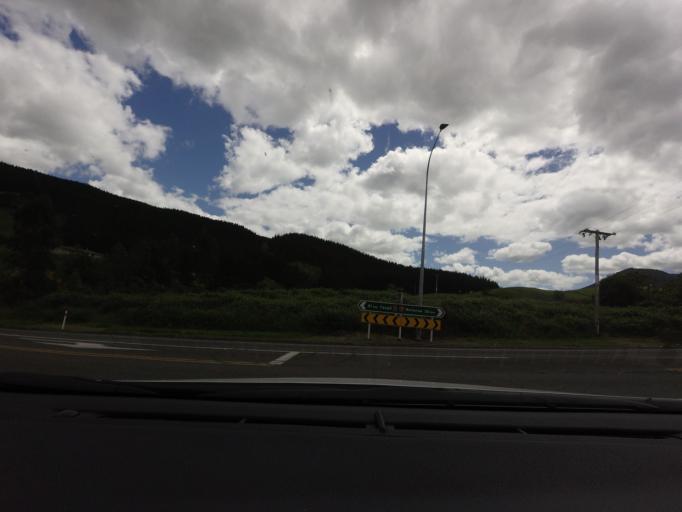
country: NZ
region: Bay of Plenty
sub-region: Rotorua District
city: Rotorua
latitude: -38.3526
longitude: 176.3615
